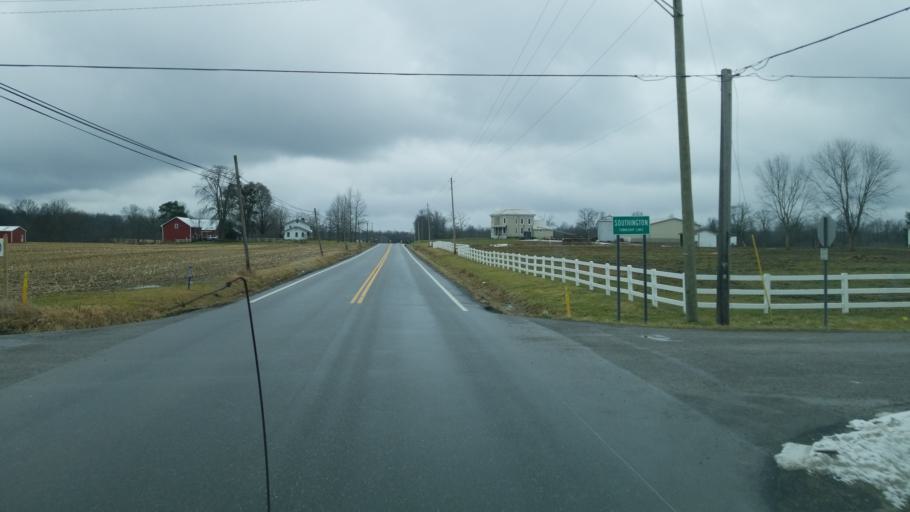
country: US
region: Ohio
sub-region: Trumbull County
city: Champion Heights
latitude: 41.3481
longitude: -80.9545
